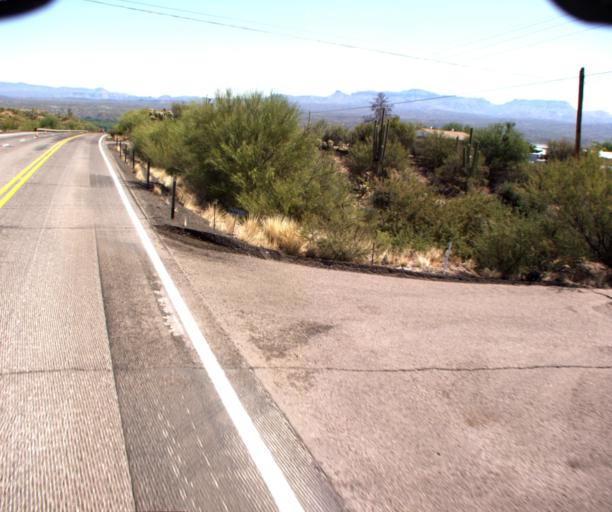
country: US
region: Arizona
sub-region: Pinal County
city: Mammoth
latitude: 32.7043
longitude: -110.6434
